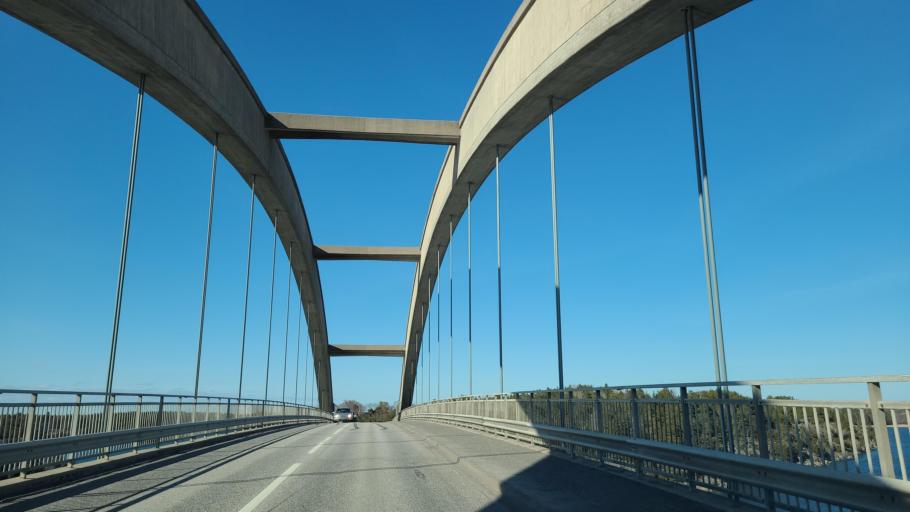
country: SE
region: Stockholm
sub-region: Varmdo Kommun
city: Holo
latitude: 59.2938
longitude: 18.6678
